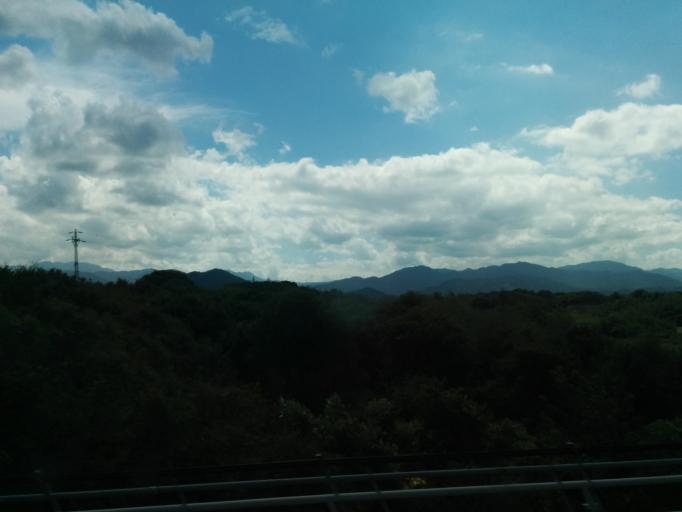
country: JP
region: Shiga Prefecture
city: Hikone
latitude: 35.2278
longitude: 136.2593
